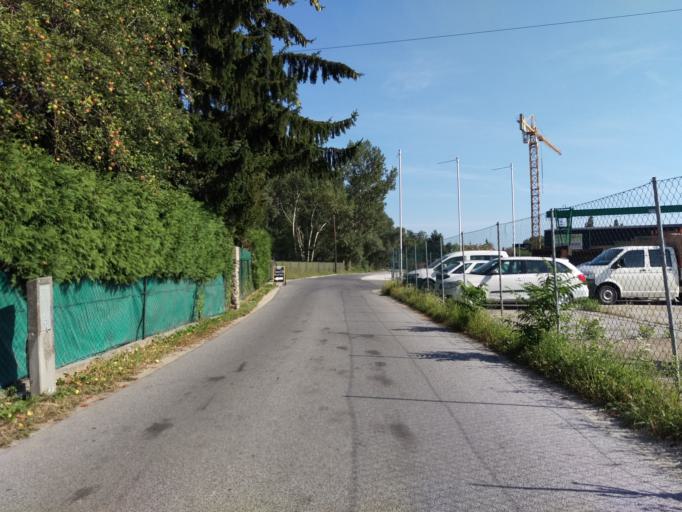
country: AT
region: Styria
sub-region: Politischer Bezirk Graz-Umgebung
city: Feldkirchen bei Graz
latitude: 47.0373
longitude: 15.4430
